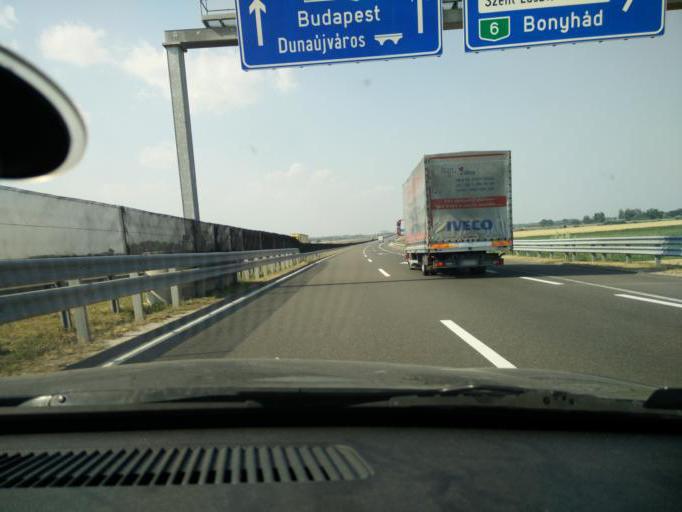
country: HU
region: Tolna
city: Szekszard
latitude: 46.3723
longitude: 18.7510
